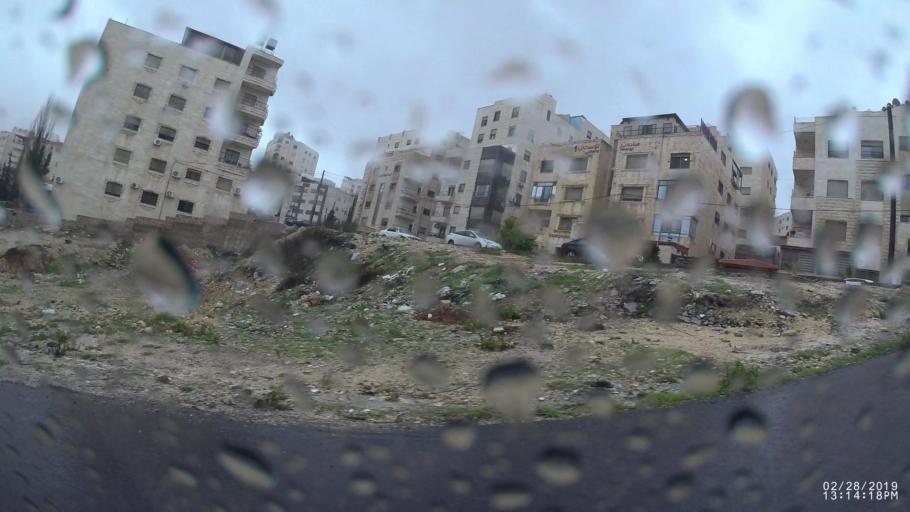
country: JO
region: Amman
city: Al Jubayhah
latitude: 32.0248
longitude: 35.8859
